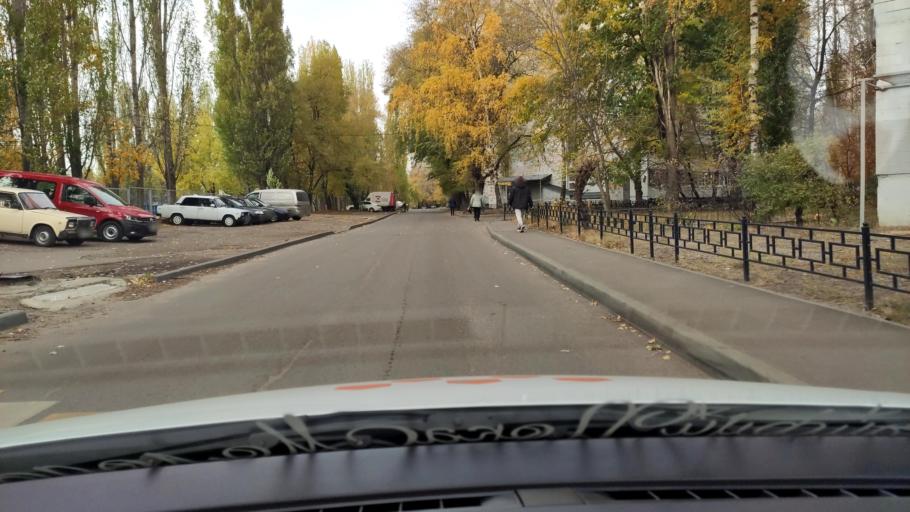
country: RU
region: Voronezj
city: Podgornoye
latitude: 51.7037
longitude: 39.1525
